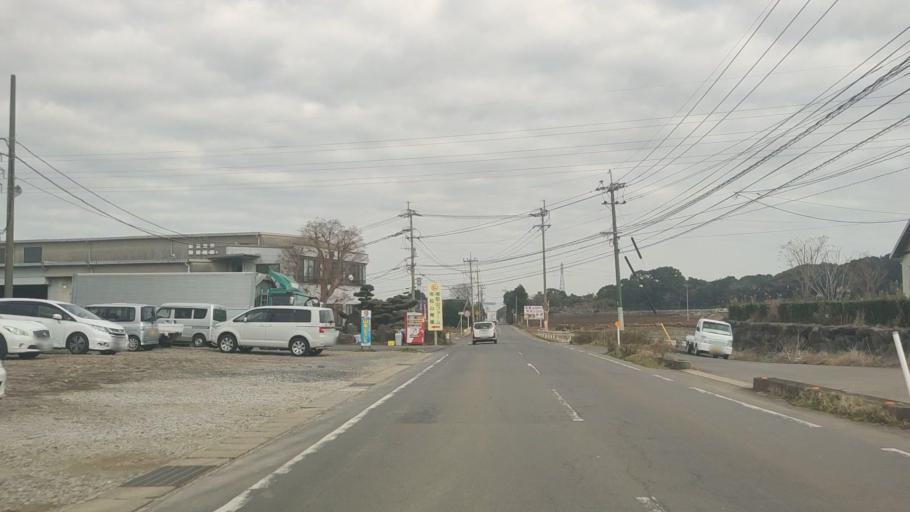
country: JP
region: Nagasaki
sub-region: Isahaya-shi
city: Isahaya
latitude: 32.8037
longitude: 130.1672
